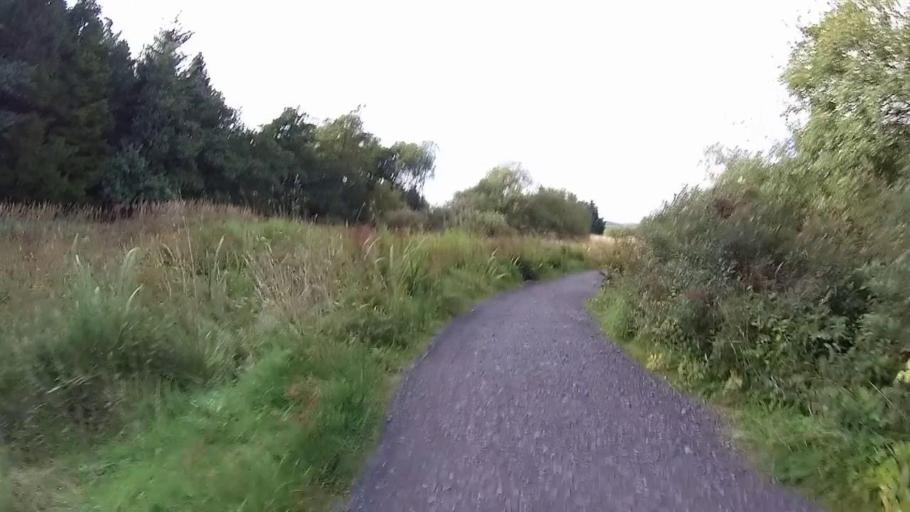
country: GB
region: Scotland
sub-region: Perth and Kinross
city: Kinross
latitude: 56.2139
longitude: -3.4039
